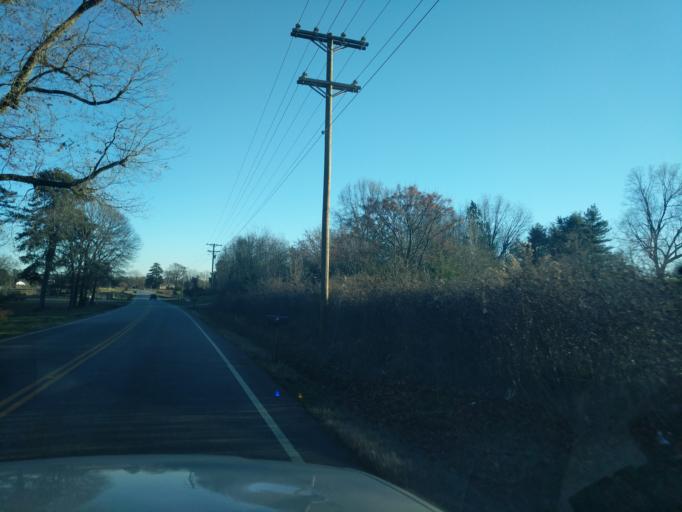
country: US
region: South Carolina
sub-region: Oconee County
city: Westminster
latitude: 34.6079
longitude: -83.0379
